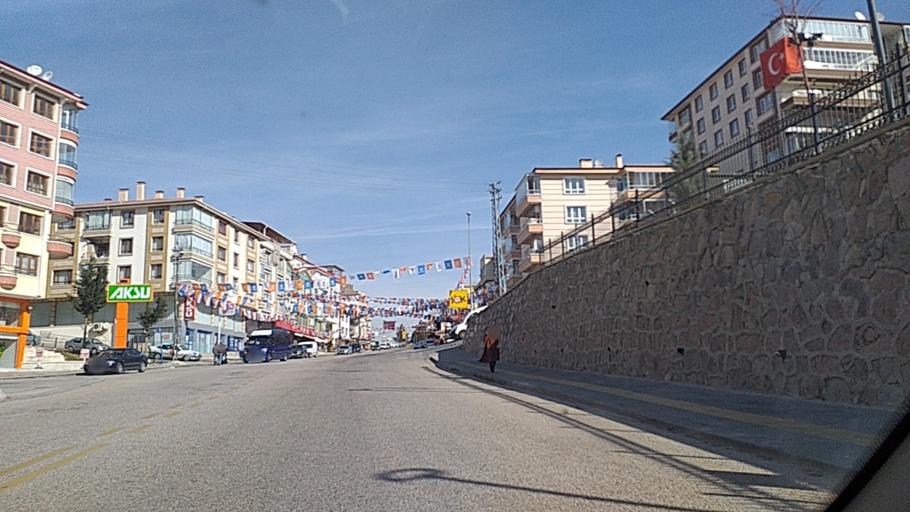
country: TR
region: Ankara
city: Batikent
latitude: 39.9930
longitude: 32.8106
